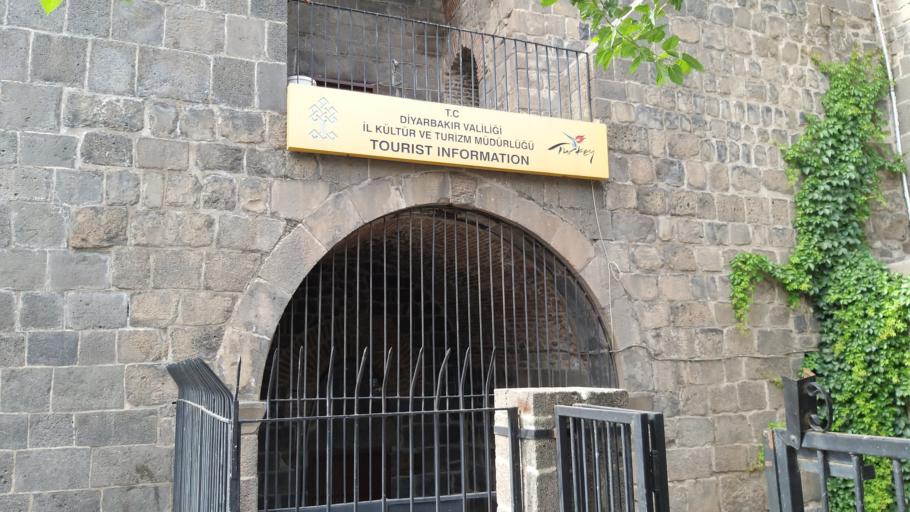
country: TR
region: Diyarbakir
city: Sur
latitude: 37.9161
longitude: 40.2367
